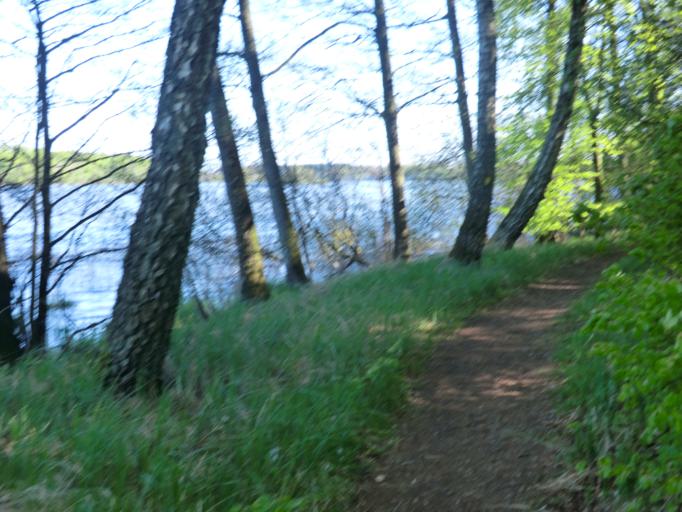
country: SE
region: Skane
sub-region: Sjobo Kommun
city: Sjoebo
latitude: 55.5716
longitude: 13.7182
